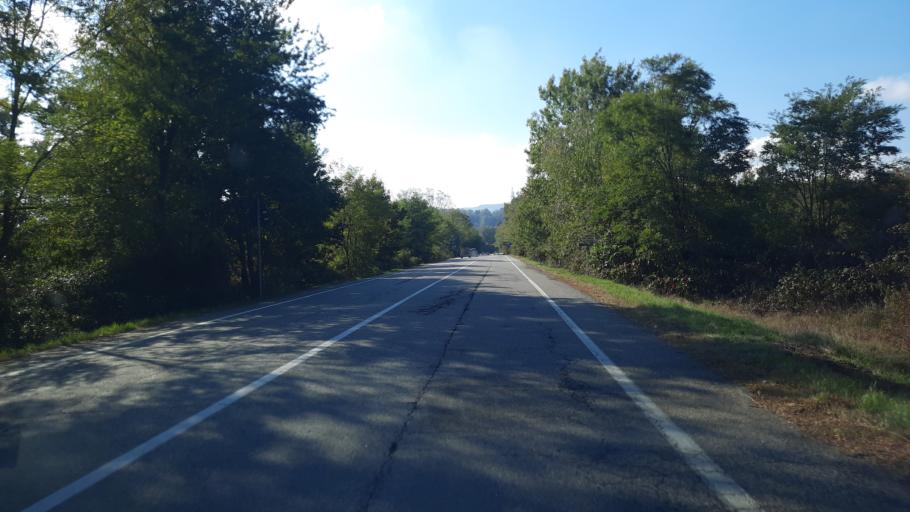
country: IT
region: Piedmont
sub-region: Provincia di Novara
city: Briga Novarese
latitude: 45.7226
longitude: 8.4462
